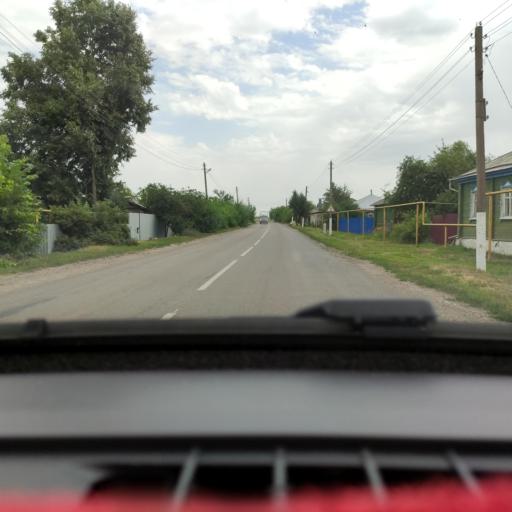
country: RU
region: Voronezj
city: Davydovka
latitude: 51.2191
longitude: 39.5265
